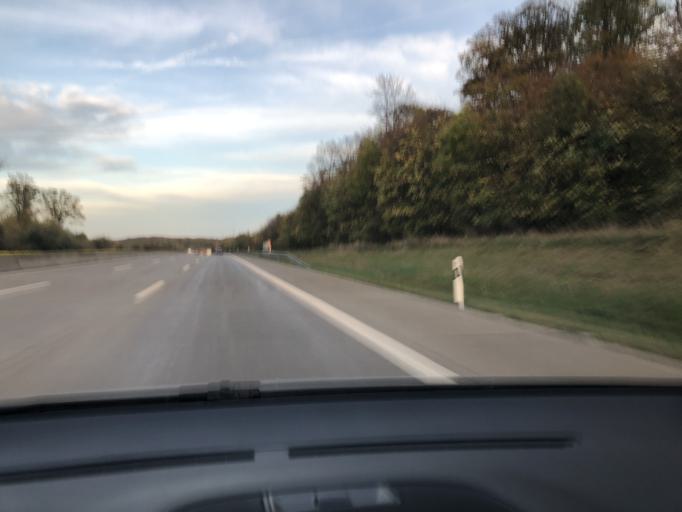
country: DE
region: Thuringia
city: Klettbach
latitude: 50.9178
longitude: 11.1054
